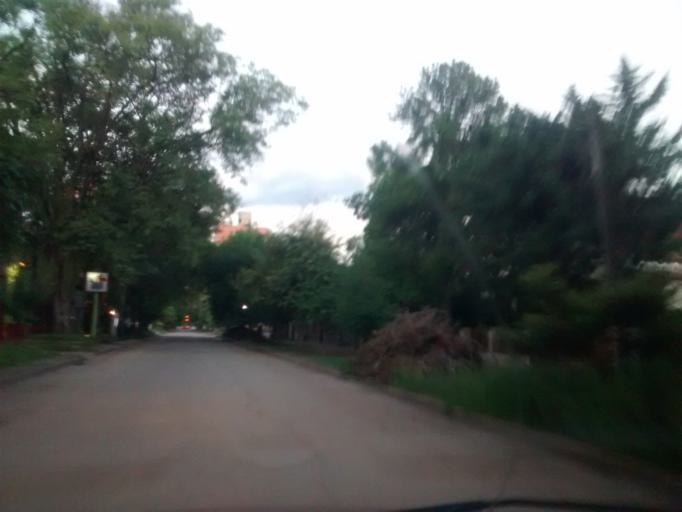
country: AR
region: Chaco
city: Resistencia
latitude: -27.4495
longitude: -58.9794
